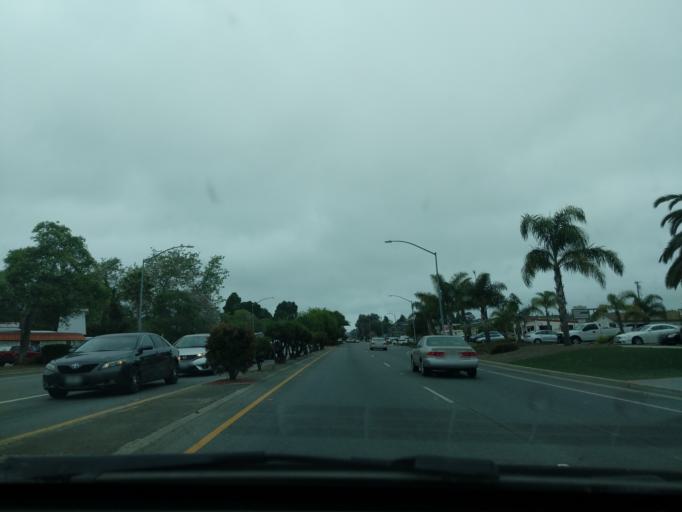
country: US
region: California
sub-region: Santa Cruz County
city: Watsonville
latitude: 36.9160
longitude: -121.7679
